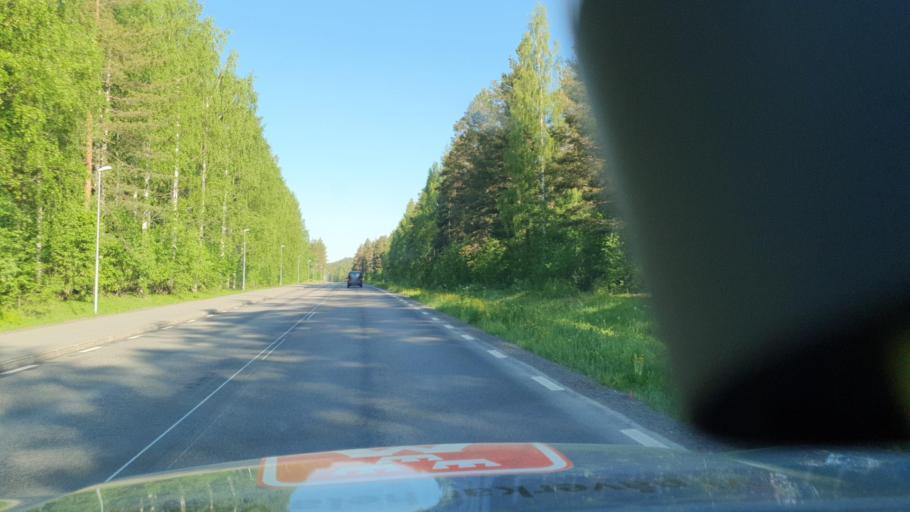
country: SE
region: Norrbotten
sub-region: Bodens Kommun
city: Boden
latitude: 65.8256
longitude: 21.6587
